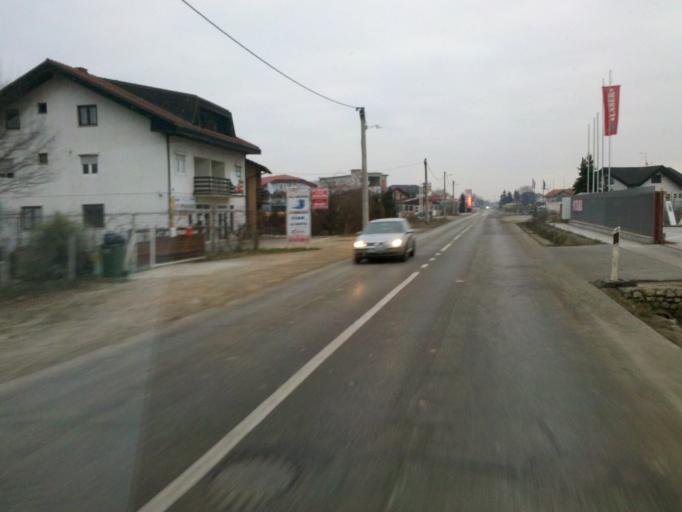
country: HR
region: Grad Zagreb
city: Lucko
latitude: 45.7575
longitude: 15.8535
